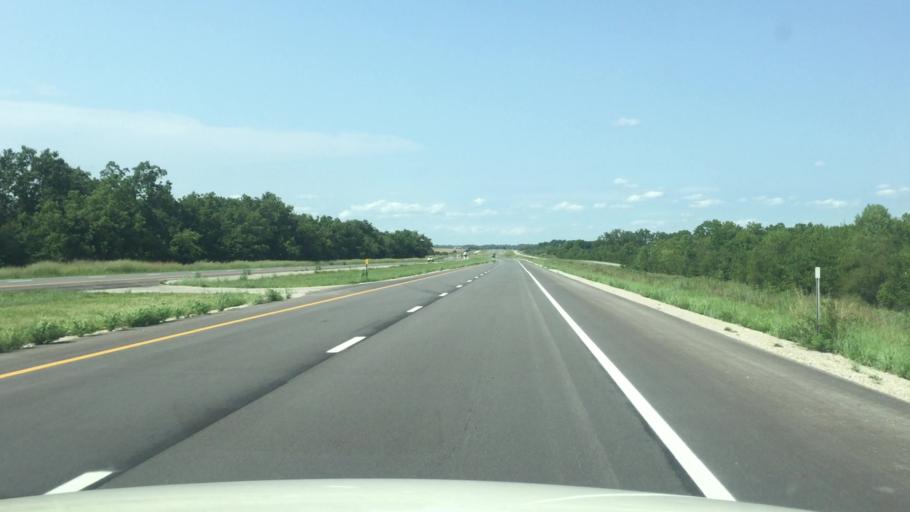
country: US
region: Kansas
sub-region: Linn County
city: La Cygne
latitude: 38.3023
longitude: -94.6773
